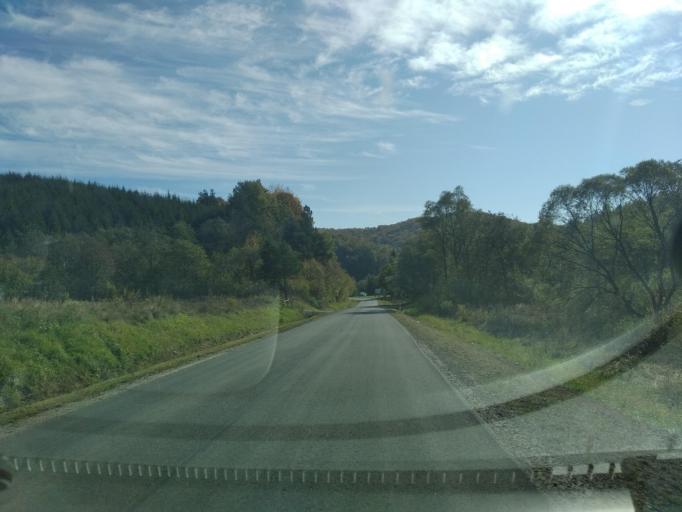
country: PL
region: Subcarpathian Voivodeship
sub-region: Powiat sanocki
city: Komancza
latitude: 49.3432
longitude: 22.0387
